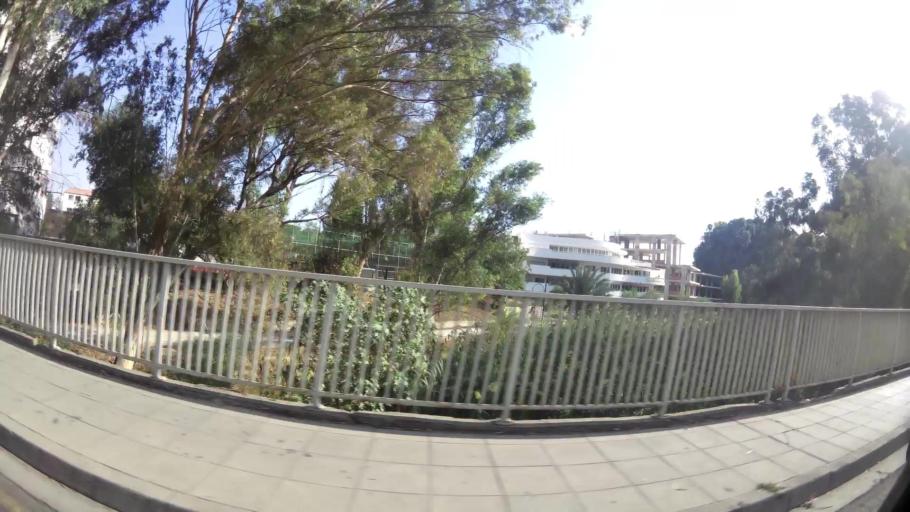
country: CY
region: Lefkosia
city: Nicosia
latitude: 35.1702
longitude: 33.3513
